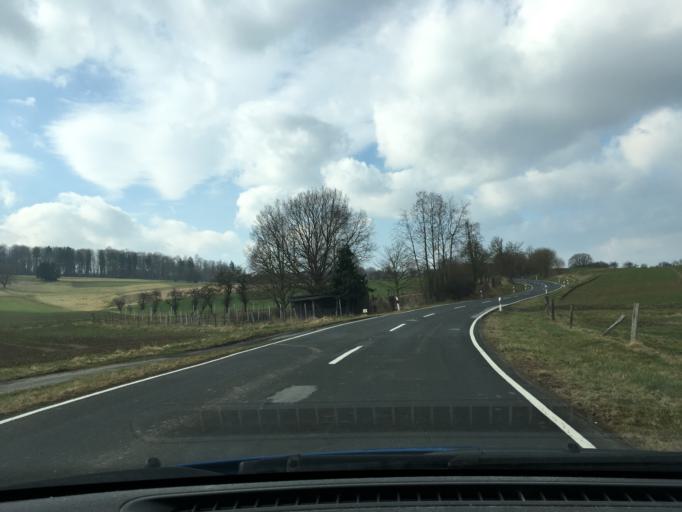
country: DE
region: Lower Saxony
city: Uslar
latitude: 51.5858
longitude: 9.6509
